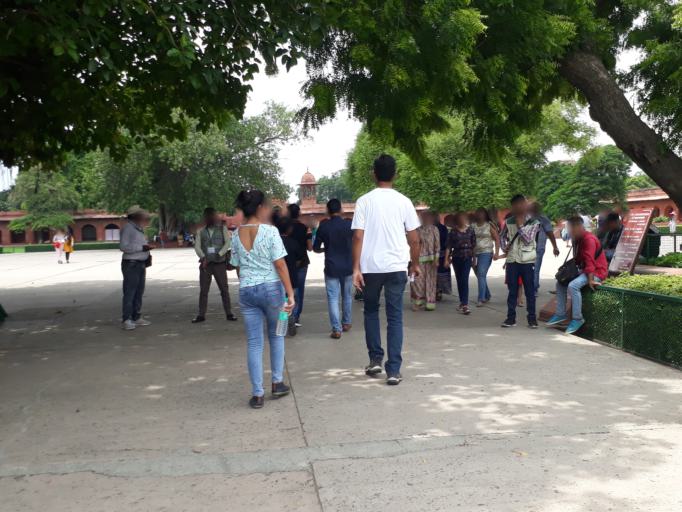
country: IN
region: Uttar Pradesh
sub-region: Agra
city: Agra
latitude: 27.1711
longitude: 78.0424
